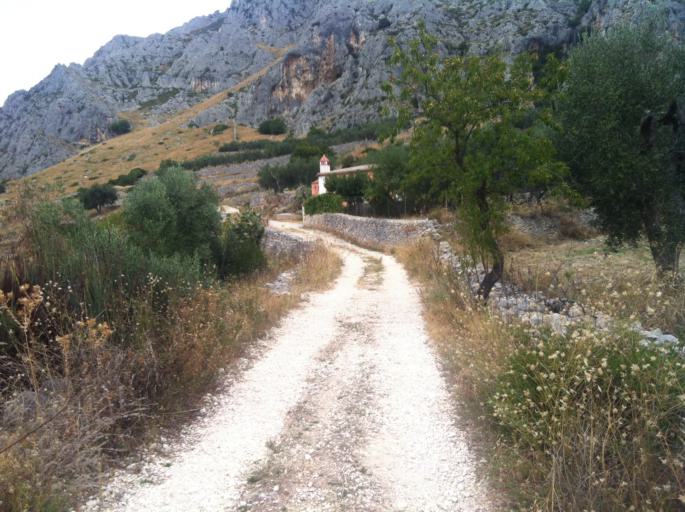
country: IT
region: Apulia
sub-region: Provincia di Foggia
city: Manfredonia
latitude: 41.6647
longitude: 15.9115
